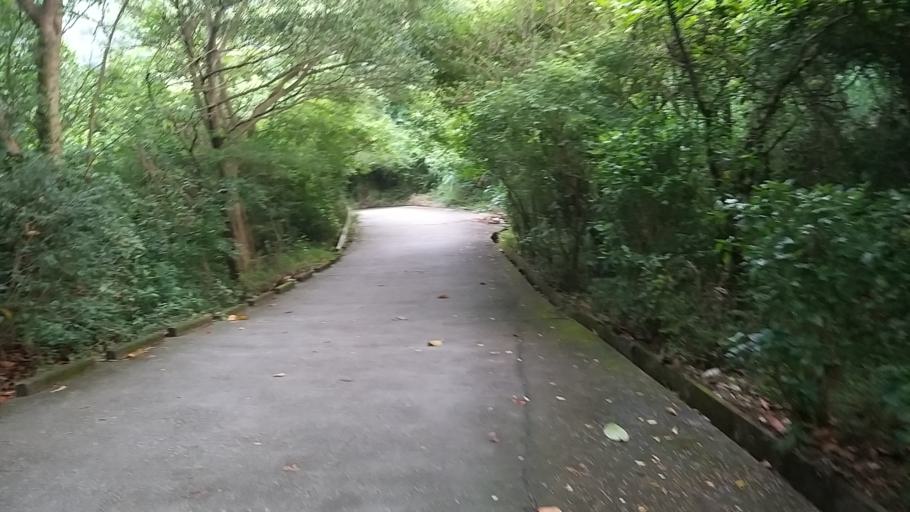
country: HK
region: Tuen Mun
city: Tuen Mun
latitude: 22.4060
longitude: 113.9532
